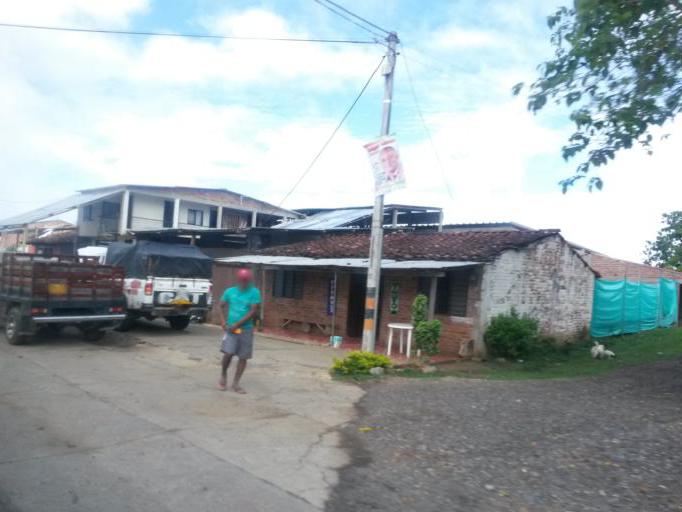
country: CO
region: Cauca
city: El Bordo
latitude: 2.1259
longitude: -76.9754
